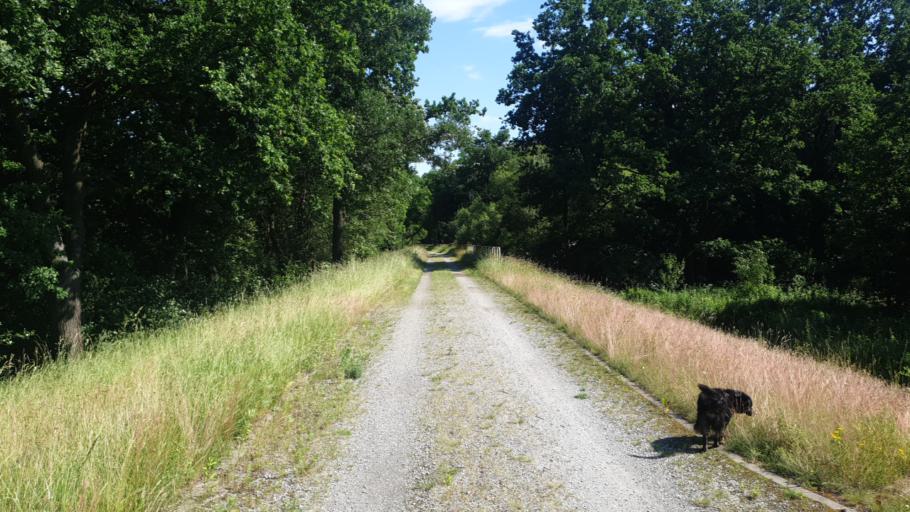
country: PL
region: Lower Silesian Voivodeship
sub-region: Powiat wroclawski
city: Radwanice
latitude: 51.0866
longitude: 17.1170
